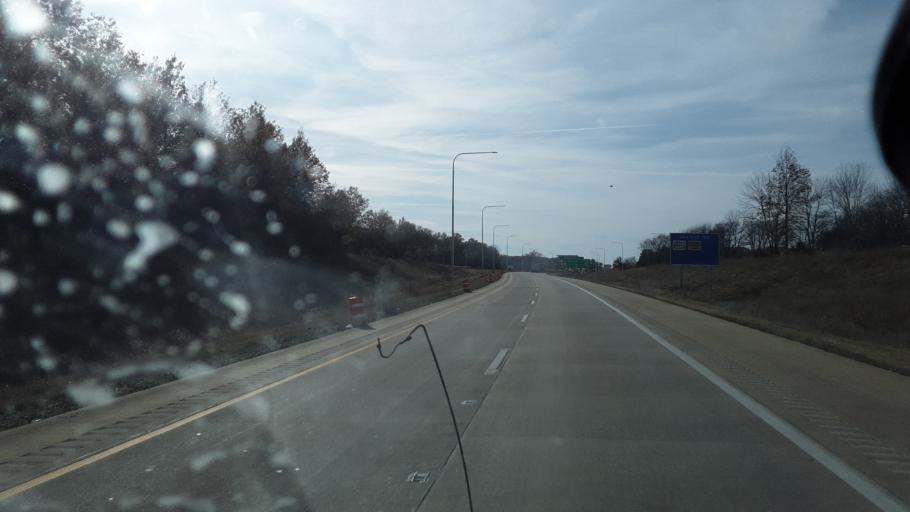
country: US
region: Illinois
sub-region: Effingham County
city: Teutopolis
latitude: 39.1491
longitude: -88.5094
